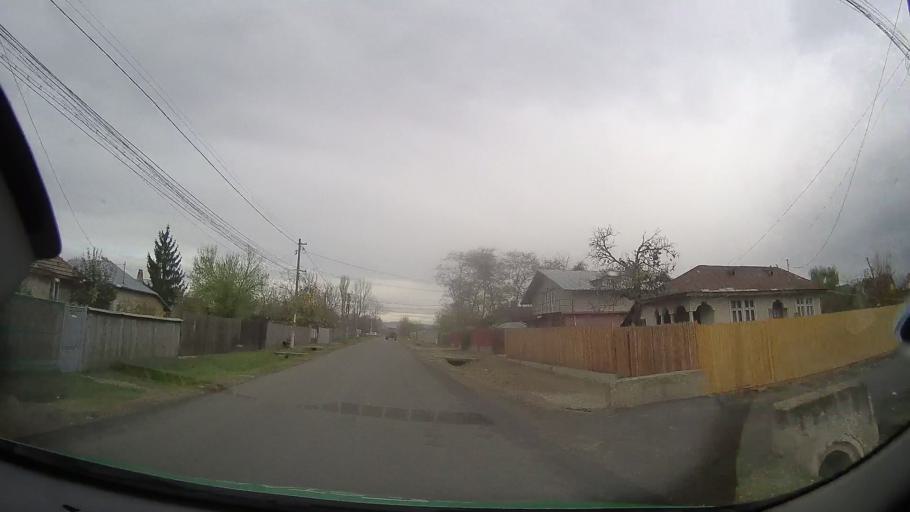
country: RO
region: Prahova
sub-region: Comuna Colceag
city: Inotesti
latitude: 44.9616
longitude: 26.3497
